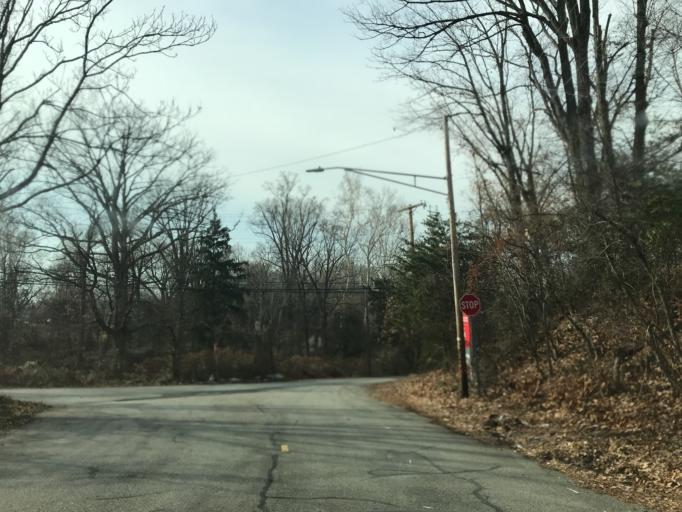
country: US
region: Maryland
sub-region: Howard County
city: Elkridge
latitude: 39.2087
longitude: -76.6916
